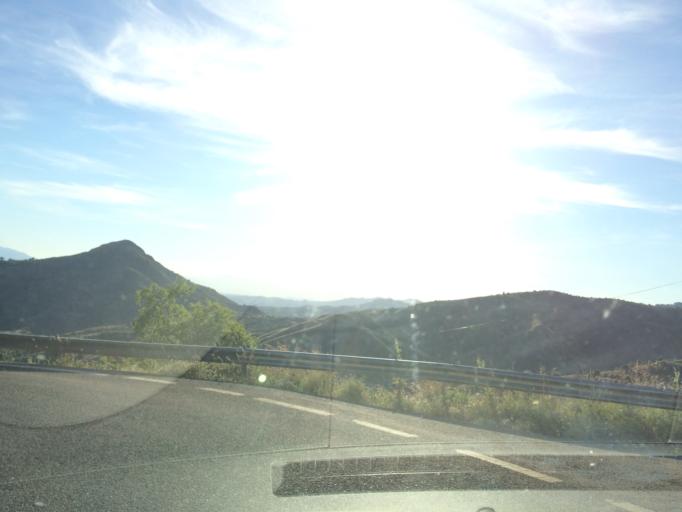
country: ES
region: Andalusia
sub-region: Provincia de Malaga
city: Totalan
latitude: 36.7521
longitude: -4.3326
